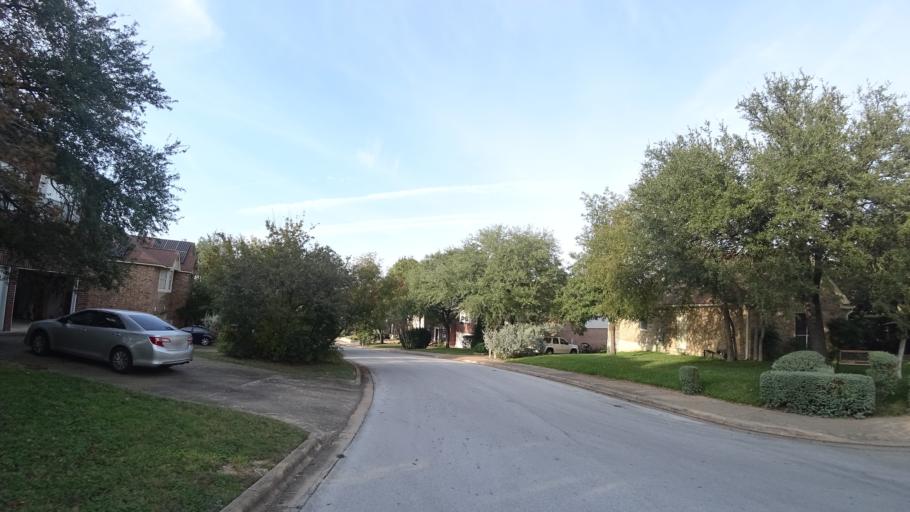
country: US
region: Texas
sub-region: Travis County
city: Hudson Bend
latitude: 30.3794
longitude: -97.8888
